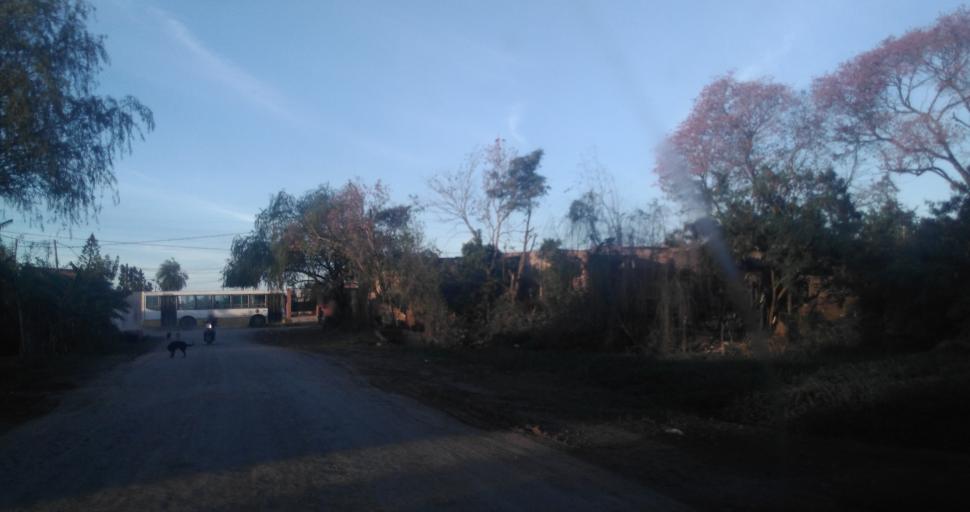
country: AR
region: Chaco
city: Fontana
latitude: -27.4294
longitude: -59.0015
